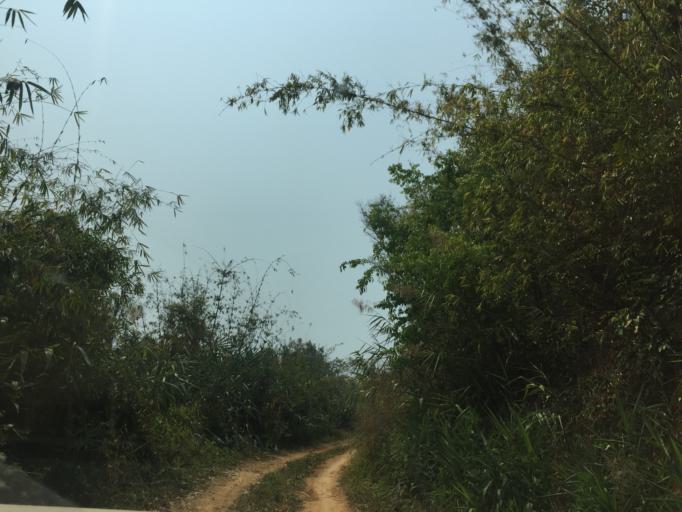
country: LA
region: Loungnamtha
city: Muang Nale
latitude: 20.6271
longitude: 101.6268
